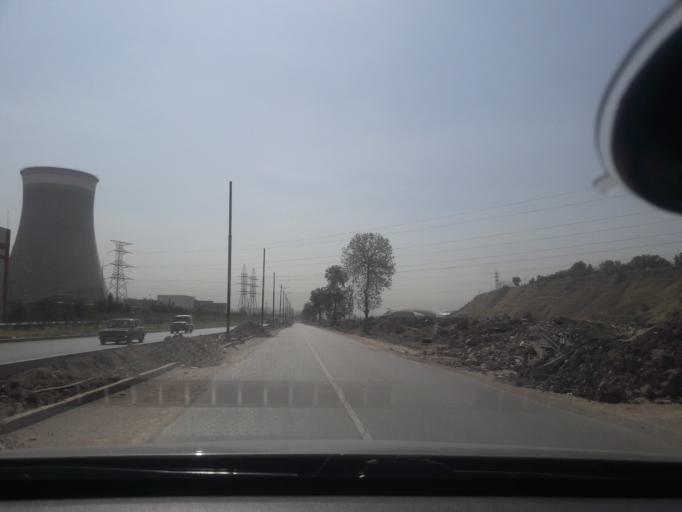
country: TJ
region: Dushanbe
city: Dushanbe
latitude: 38.6108
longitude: 68.7705
